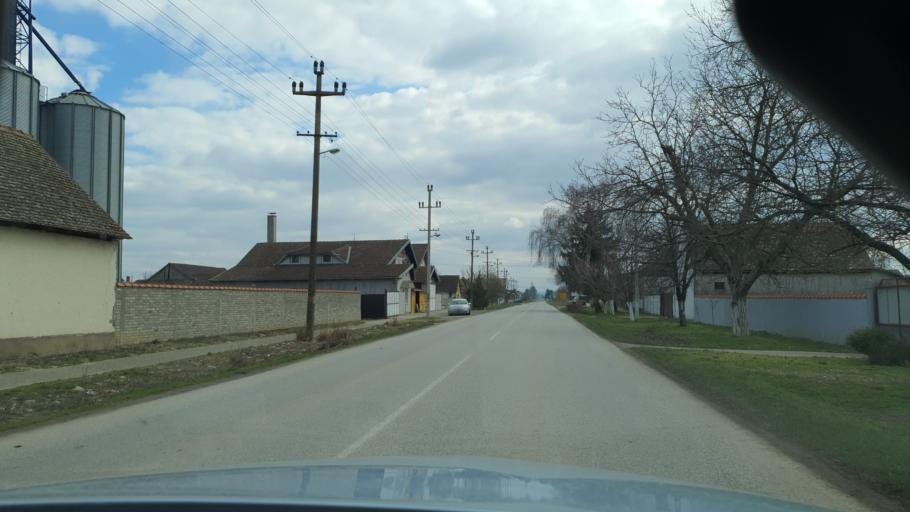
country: RS
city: Maglic
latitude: 45.3959
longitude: 19.4559
